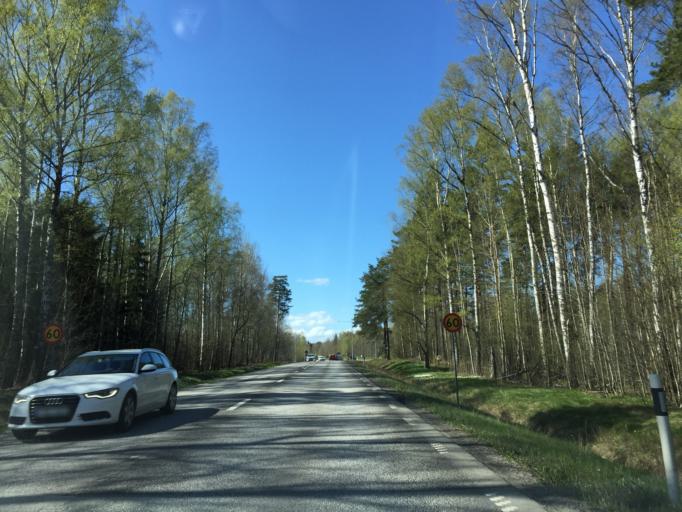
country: SE
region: OErebro
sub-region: Hallsbergs Kommun
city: Skollersta
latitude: 59.1333
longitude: 15.2867
